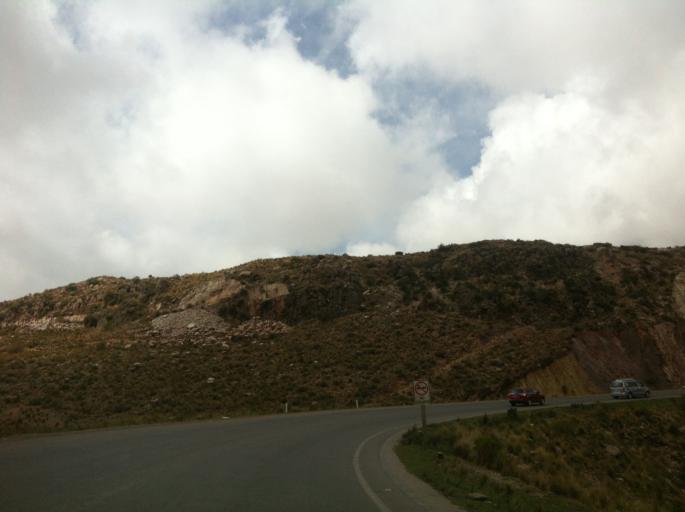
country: BO
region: Cochabamba
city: Irpa Irpa
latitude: -17.6908
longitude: -66.4799
